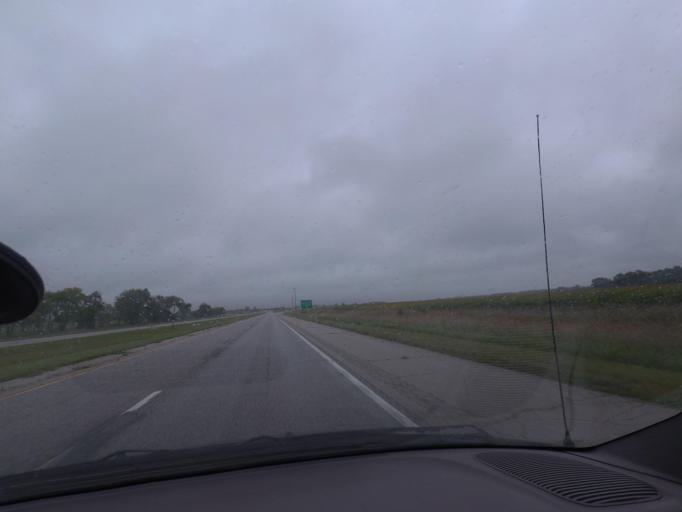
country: US
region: Illinois
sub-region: Pike County
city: Pittsfield
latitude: 39.6722
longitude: -90.8465
